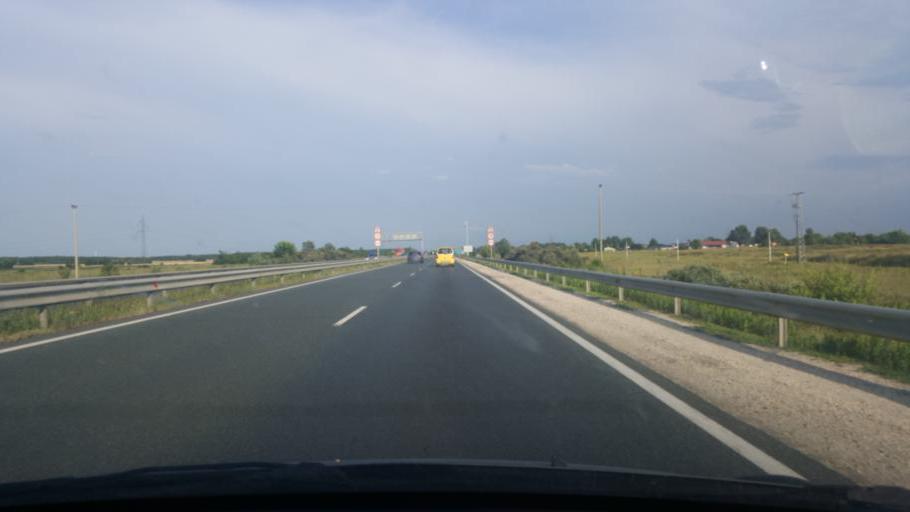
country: HU
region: Pest
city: Ullo
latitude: 47.3993
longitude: 19.3576
